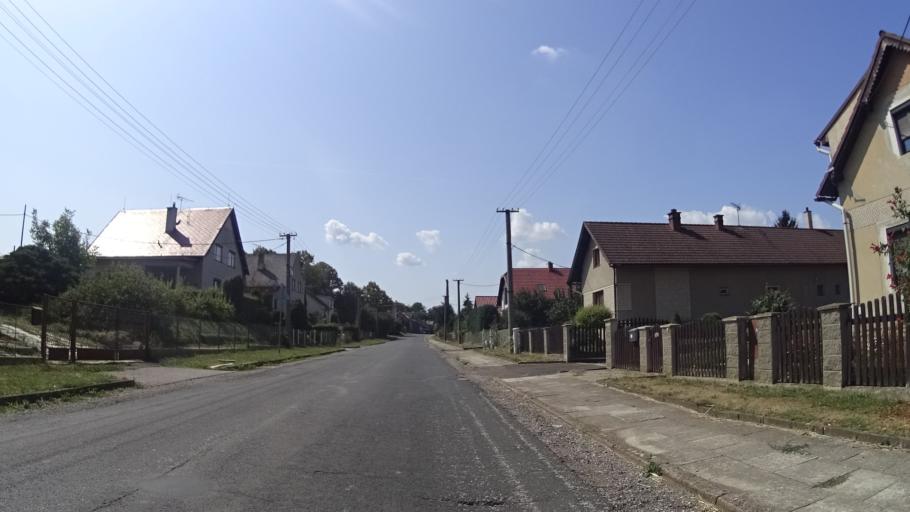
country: CZ
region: Kralovehradecky
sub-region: Okres Jicin
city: Jicin
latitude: 50.3692
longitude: 15.3863
